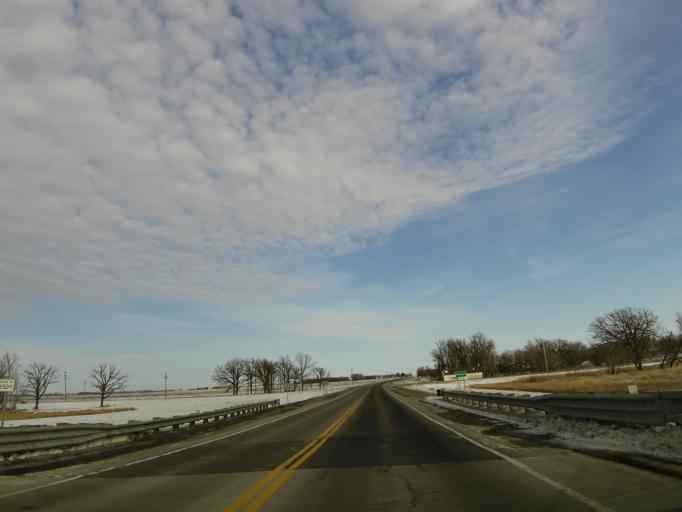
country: US
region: Minnesota
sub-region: Kittson County
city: Hallock
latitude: 48.5726
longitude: -97.1451
